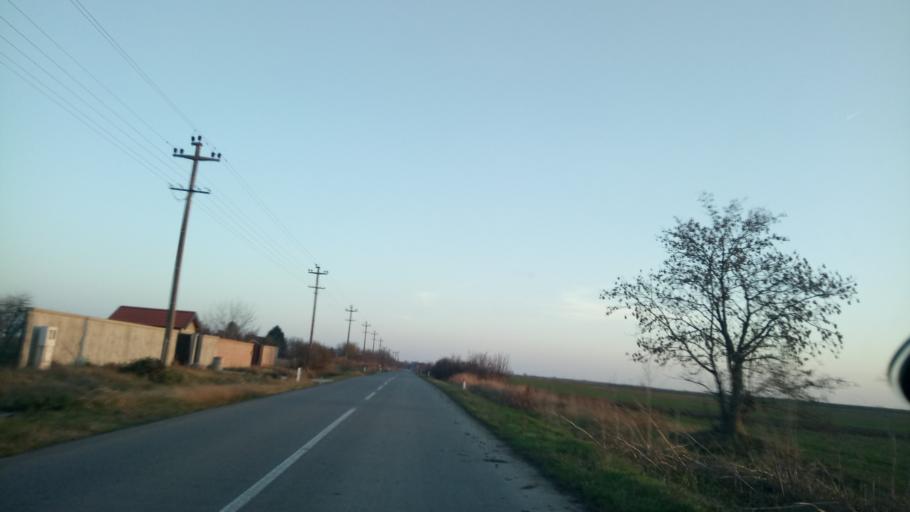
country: RS
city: Surduk
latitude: 45.0905
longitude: 20.3001
